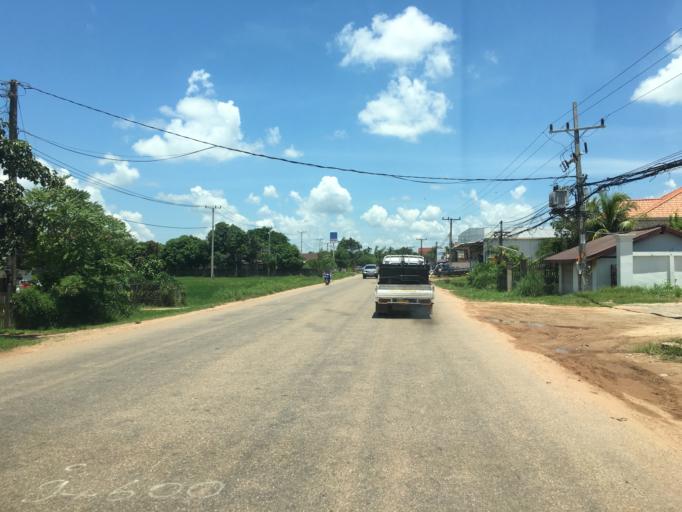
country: LA
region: Vientiane
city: Vientiane
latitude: 18.1022
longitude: 102.5102
